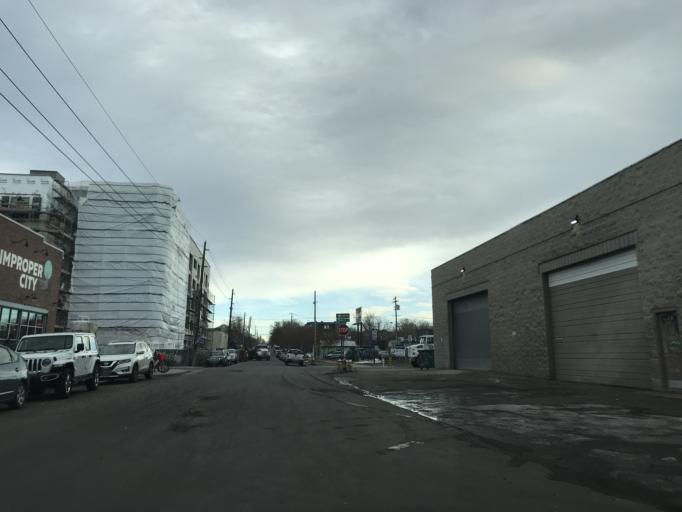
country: US
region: Colorado
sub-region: Denver County
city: Denver
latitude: 39.7651
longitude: -104.9794
